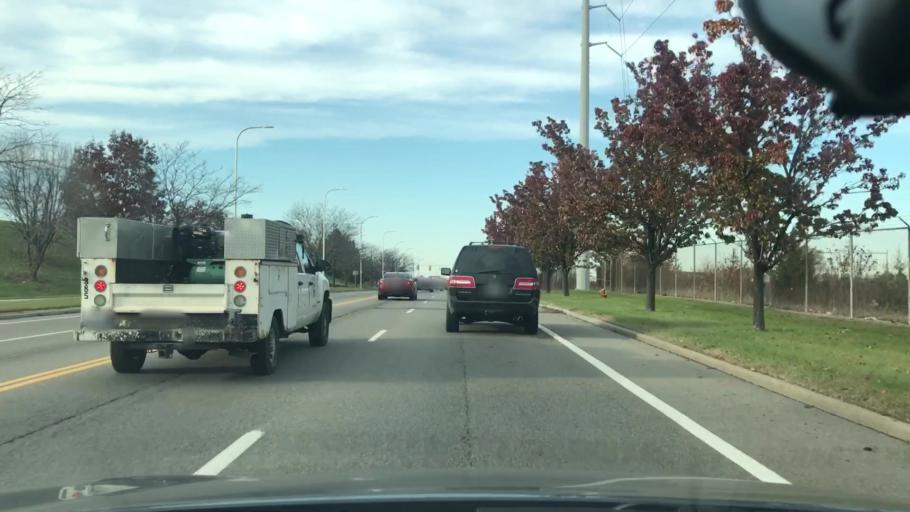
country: US
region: Michigan
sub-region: Wayne County
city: Grosse Pointe Park
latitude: 42.3771
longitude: -82.9771
